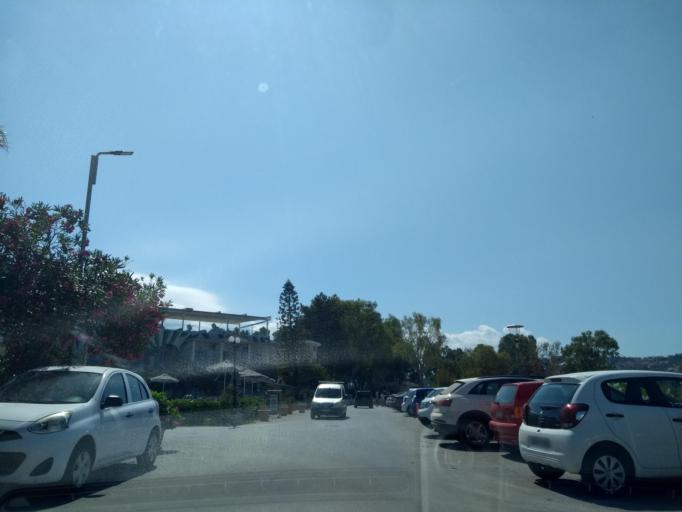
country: GR
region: Crete
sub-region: Nomos Chanias
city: Georgioupolis
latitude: 35.3636
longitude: 24.2618
